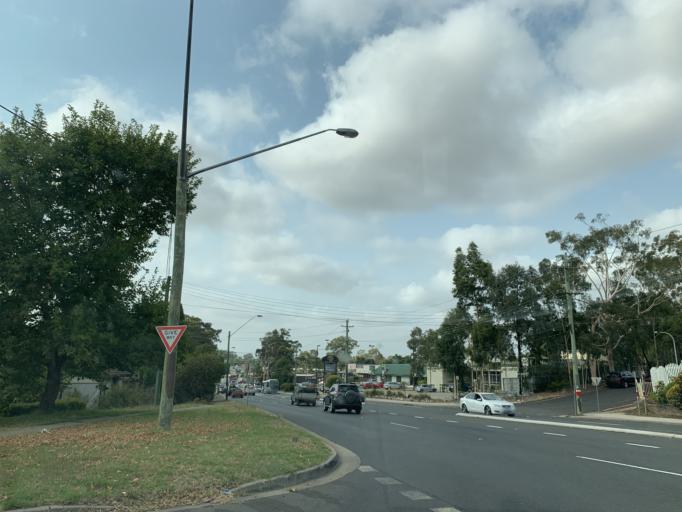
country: AU
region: New South Wales
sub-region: Blacktown
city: Blacktown
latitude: -33.7767
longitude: 150.9202
